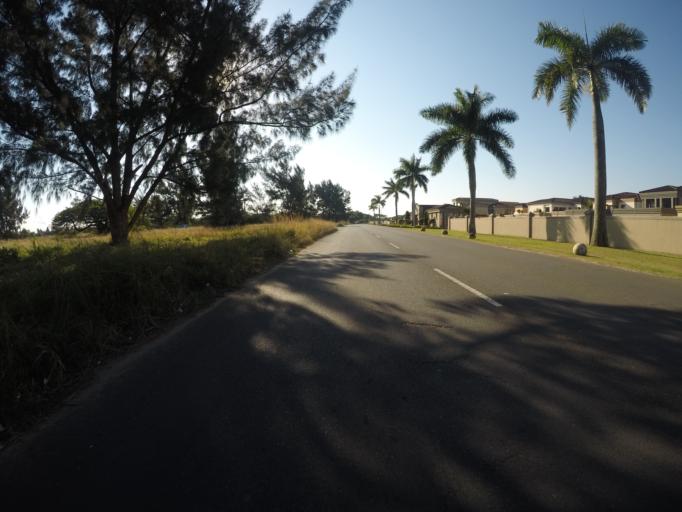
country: ZA
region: KwaZulu-Natal
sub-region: uThungulu District Municipality
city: Richards Bay
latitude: -28.7893
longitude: 32.0805
